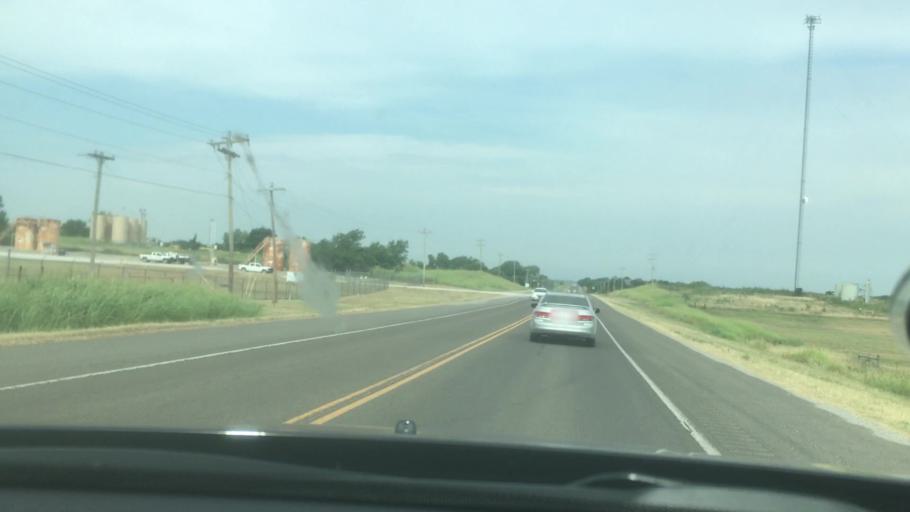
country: US
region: Oklahoma
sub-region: Garvin County
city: Maysville
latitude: 34.8192
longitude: -97.4476
